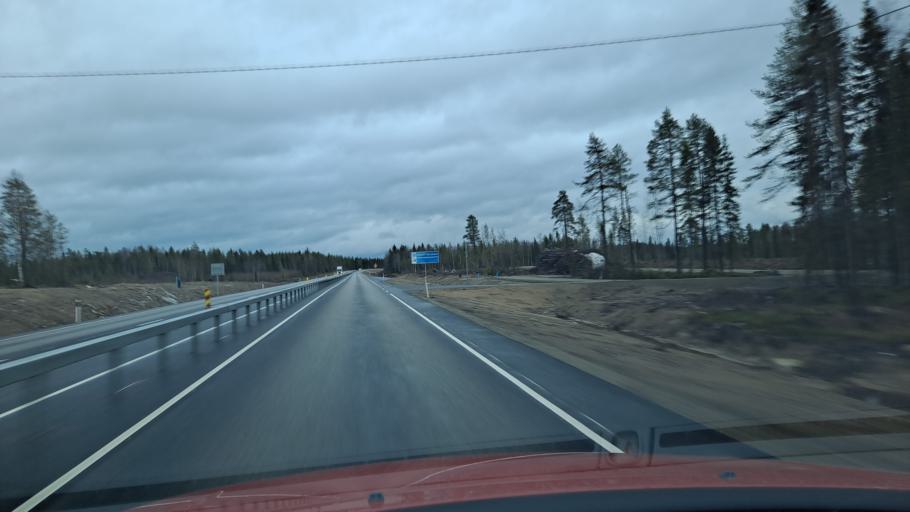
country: FI
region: Northern Ostrobothnia
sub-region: Oulunkaari
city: Kuivaniemi
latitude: 65.6235
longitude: 25.1468
